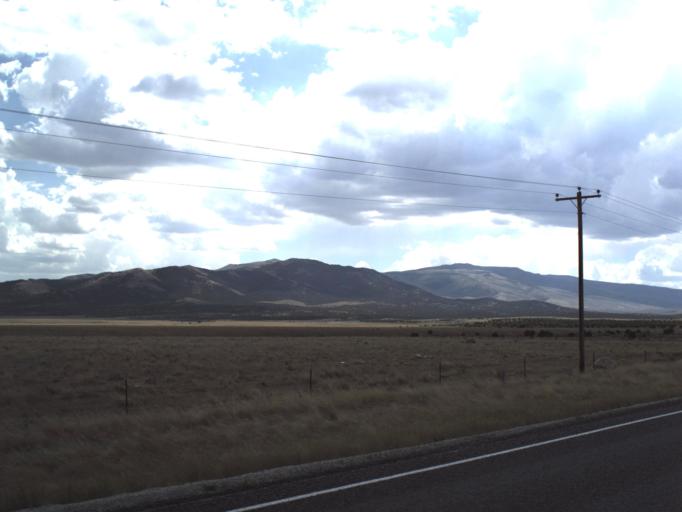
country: US
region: Idaho
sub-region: Minidoka County
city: Rupert
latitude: 41.9708
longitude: -113.1312
